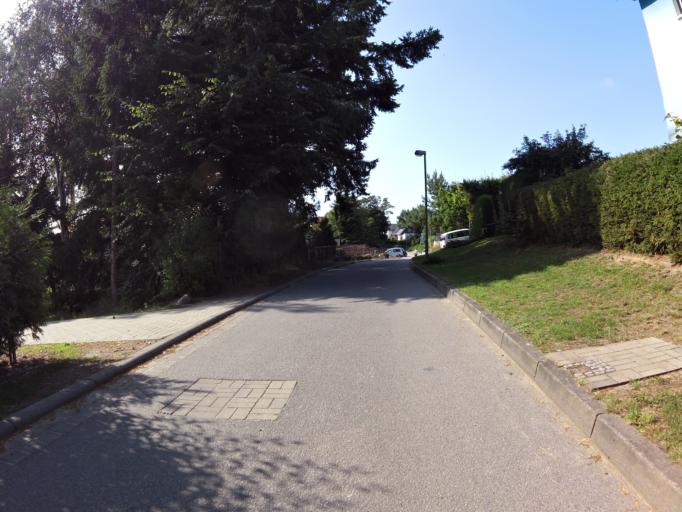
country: DE
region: Mecklenburg-Vorpommern
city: Seebad Bansin
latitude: 53.9609
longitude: 14.1340
